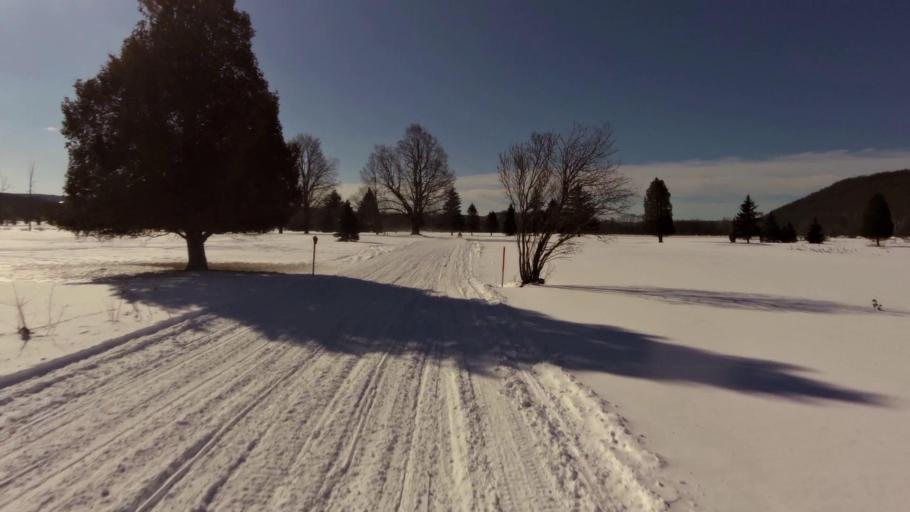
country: US
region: New York
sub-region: Cattaraugus County
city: Franklinville
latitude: 42.3589
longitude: -78.4565
